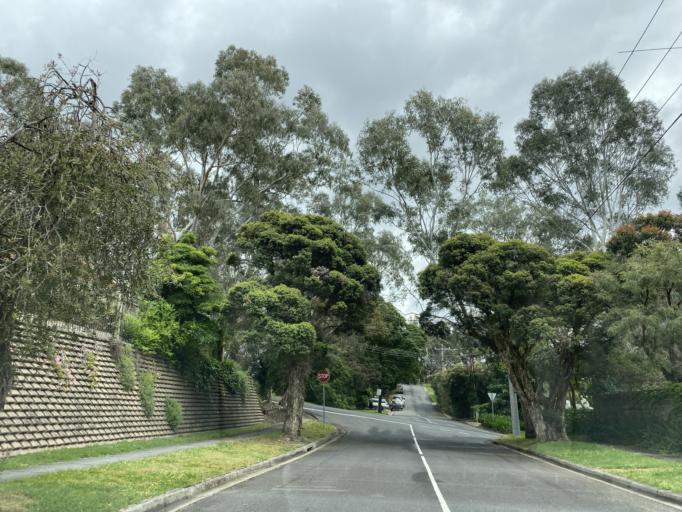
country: AU
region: Victoria
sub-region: Banyule
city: Darch
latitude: -37.7523
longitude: 145.1266
